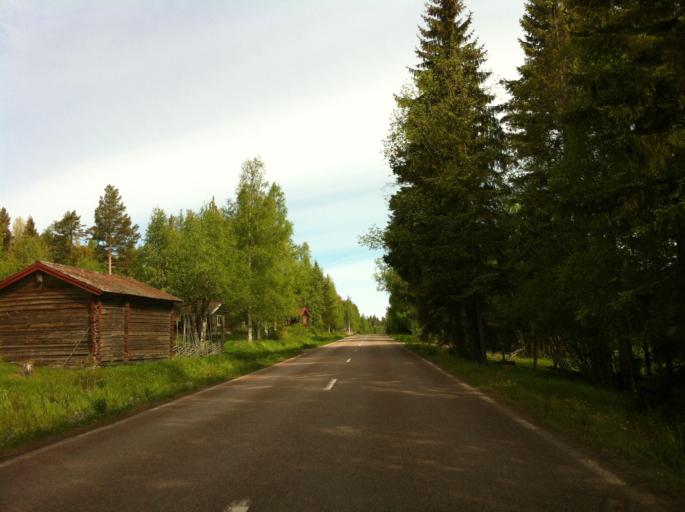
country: SE
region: Dalarna
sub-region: Leksand Municipality
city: Siljansnas
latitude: 60.8004
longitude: 14.6785
